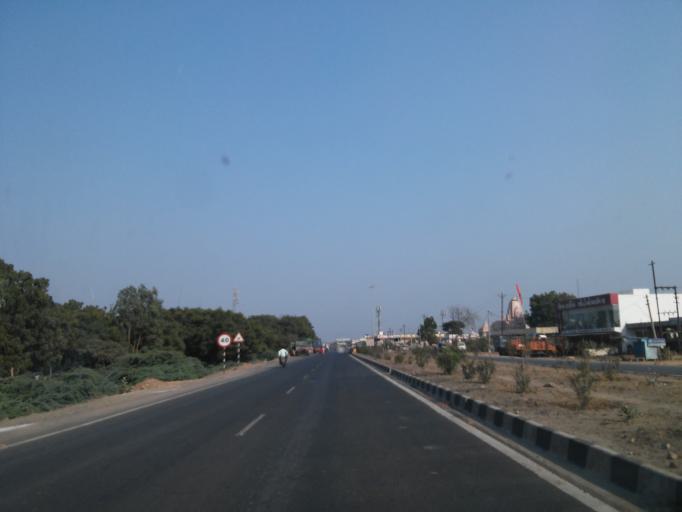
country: IN
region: Gujarat
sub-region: Surendranagar
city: Halvad
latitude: 23.0035
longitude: 71.1830
